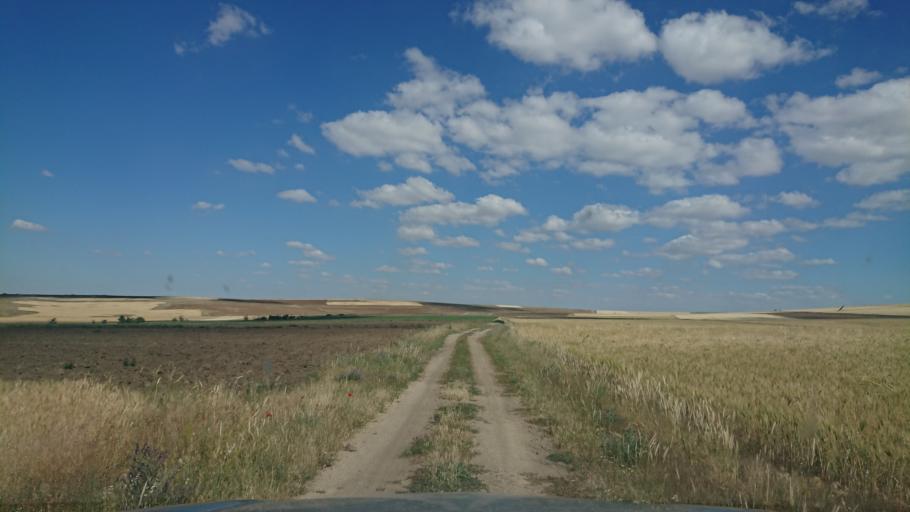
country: TR
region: Aksaray
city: Sariyahsi
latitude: 38.9395
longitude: 33.8356
